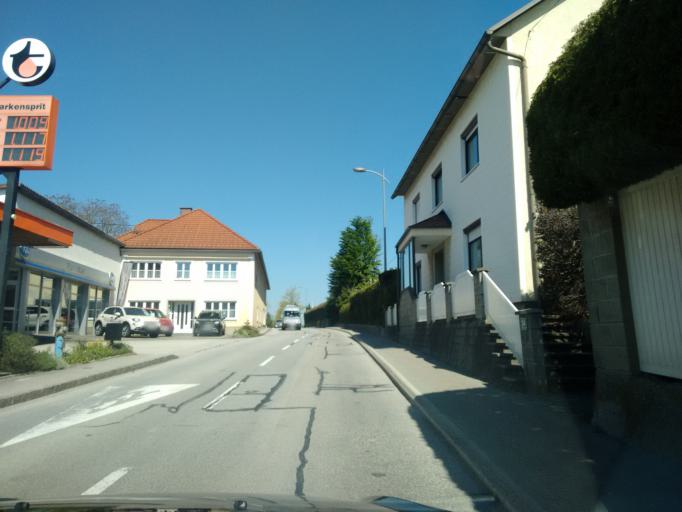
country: AT
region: Upper Austria
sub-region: Politischer Bezirk Steyr-Land
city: Waldneukirchen
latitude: 47.9988
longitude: 14.2598
